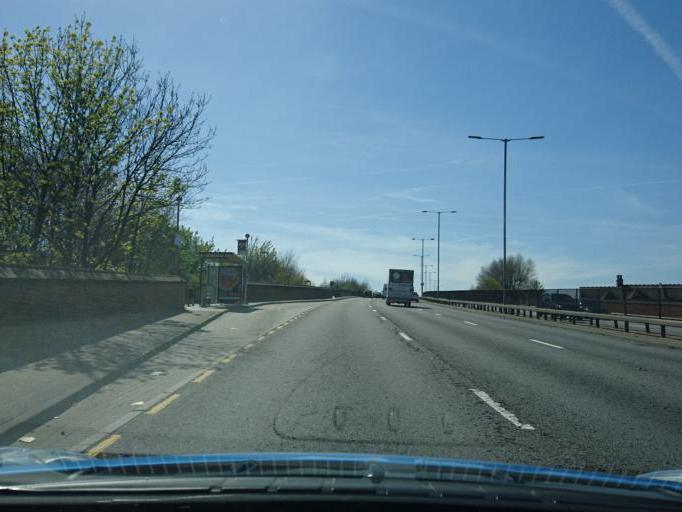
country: GB
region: England
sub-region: Greater London
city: Hendon
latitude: 51.5979
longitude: -0.1782
